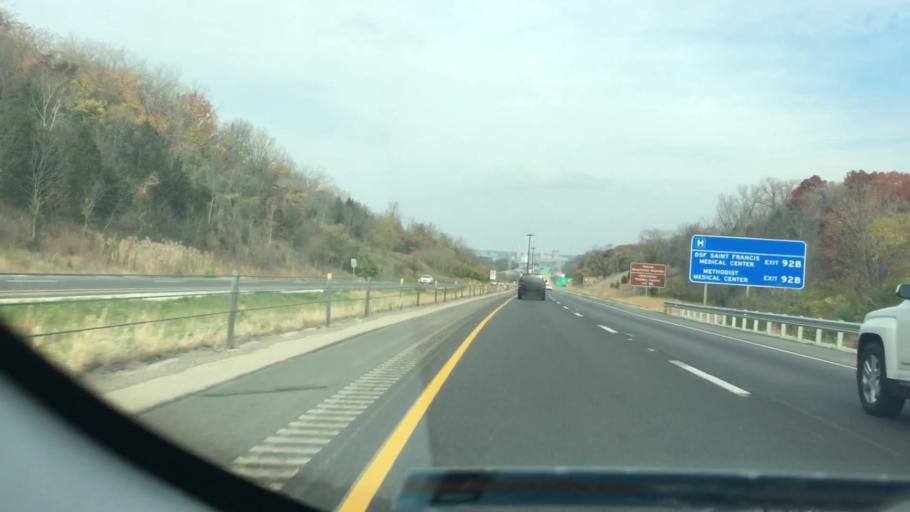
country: US
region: Illinois
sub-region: Tazewell County
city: East Peoria
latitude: 40.6547
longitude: -89.5622
